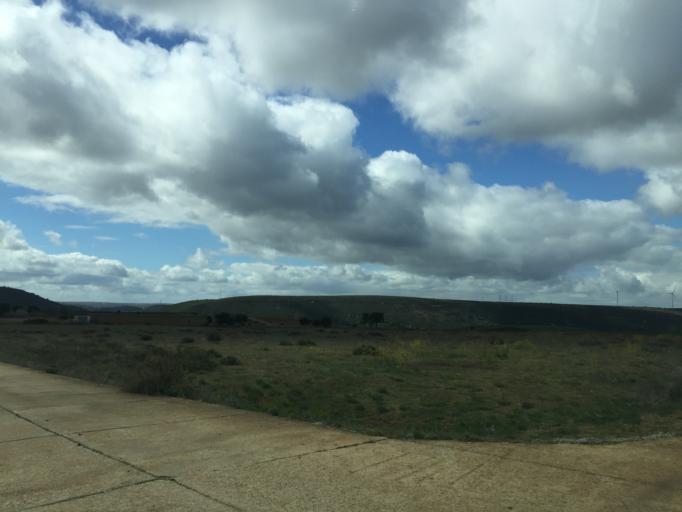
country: ES
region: Castille and Leon
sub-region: Provincia de Zamora
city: Manzanal del Barco
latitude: 41.5854
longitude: -5.9655
